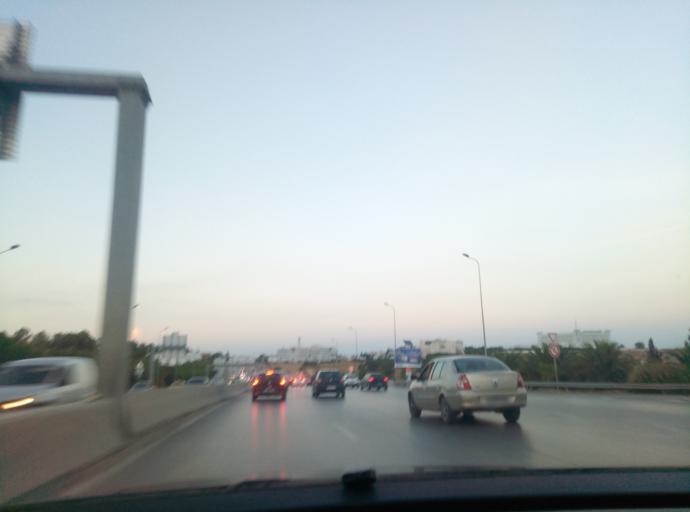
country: TN
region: Tunis
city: Tunis
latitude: 36.8271
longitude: 10.1469
